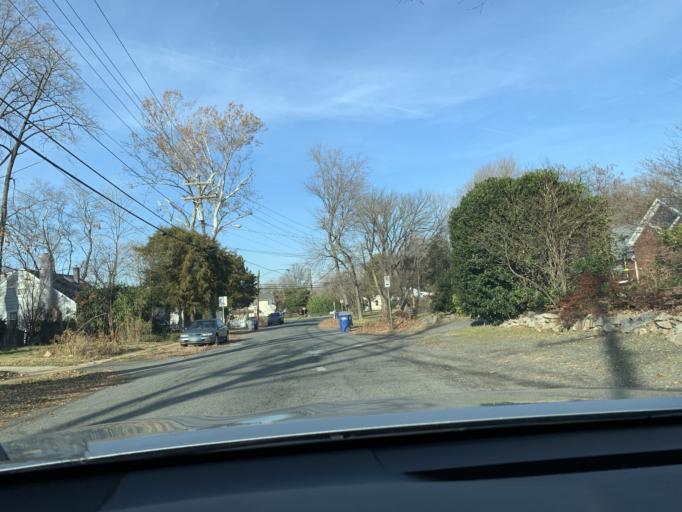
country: US
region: Virginia
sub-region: Fairfax County
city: Jefferson
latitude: 38.8562
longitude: -77.1850
